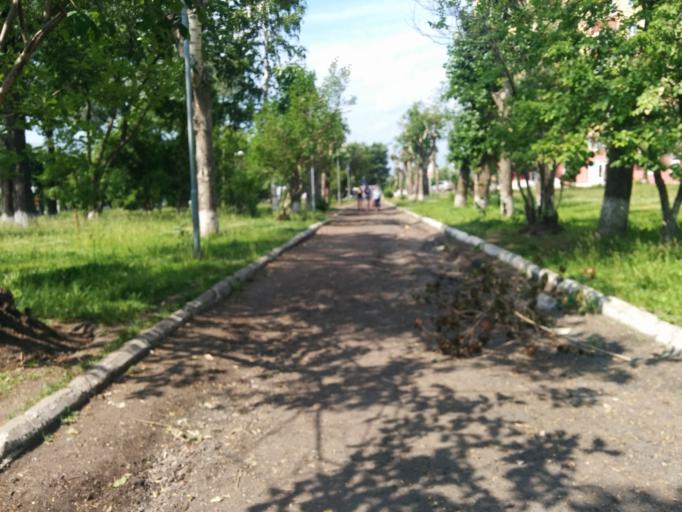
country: RU
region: Perm
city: Perm
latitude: 58.0213
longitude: 56.2867
